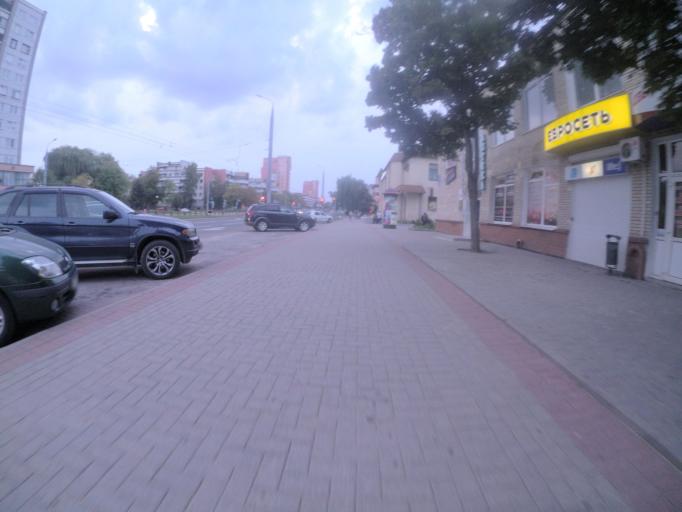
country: BY
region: Grodnenskaya
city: Hrodna
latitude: 53.6929
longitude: 23.8241
